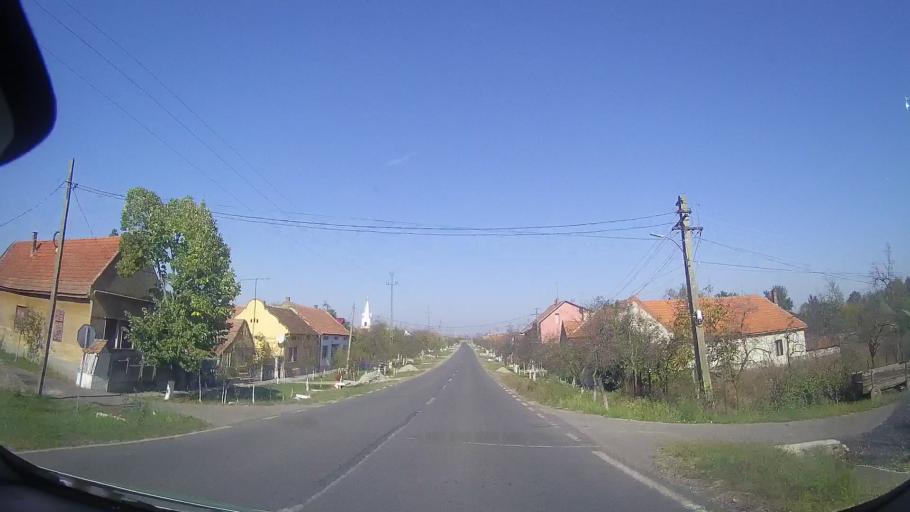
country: RO
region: Timis
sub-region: Comuna Costeiu
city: Costeiu
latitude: 45.7748
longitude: 21.8496
